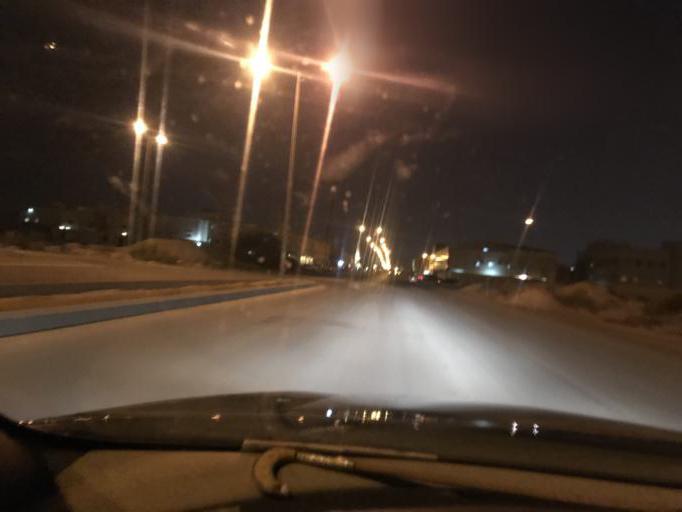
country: SA
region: Ar Riyad
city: Riyadh
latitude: 24.8175
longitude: 46.7216
